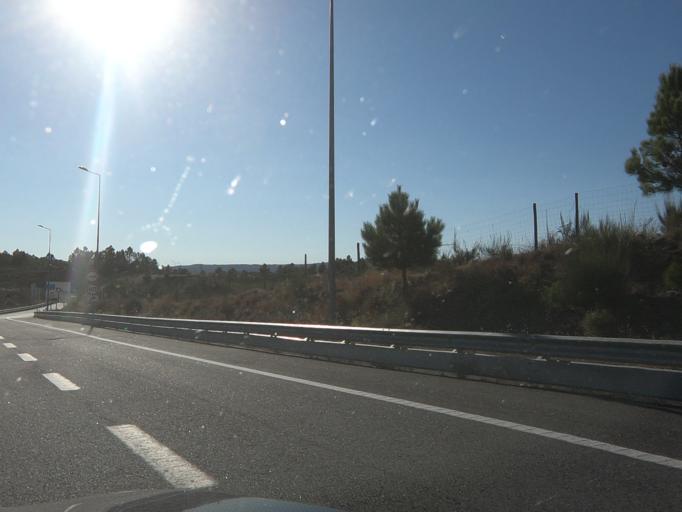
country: PT
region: Vila Real
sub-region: Murca
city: Murca
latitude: 41.4198
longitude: -7.4085
